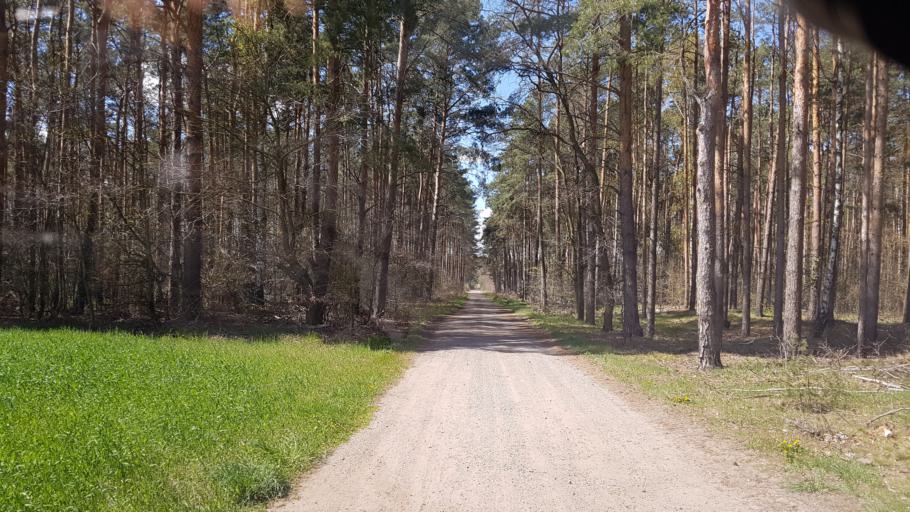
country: DE
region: Brandenburg
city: Bad Liebenwerda
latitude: 51.5230
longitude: 13.4290
